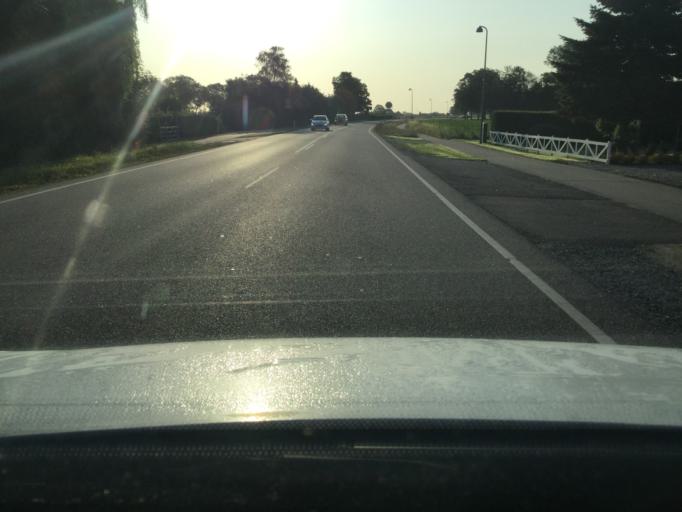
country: DK
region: Zealand
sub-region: Lolland Kommune
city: Nakskov
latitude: 54.8111
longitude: 11.2069
